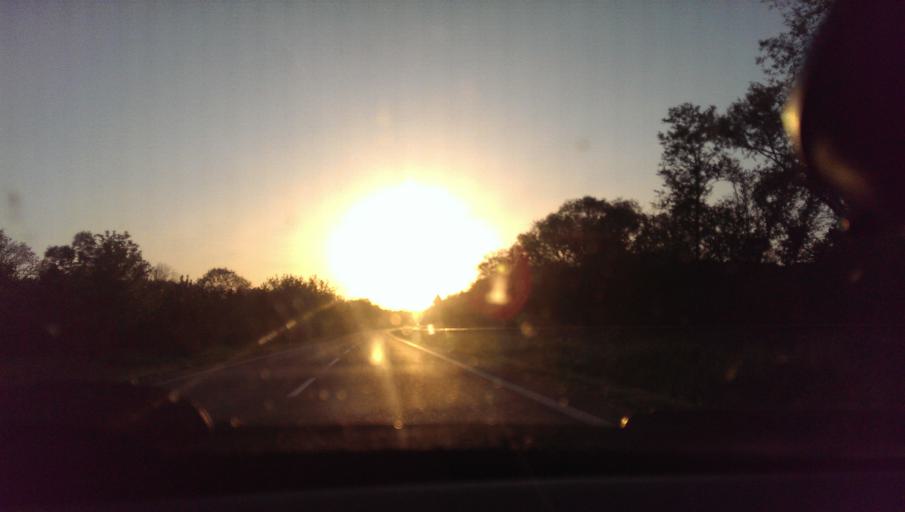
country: CZ
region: Zlin
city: Zasova
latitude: 49.4704
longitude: 18.0284
